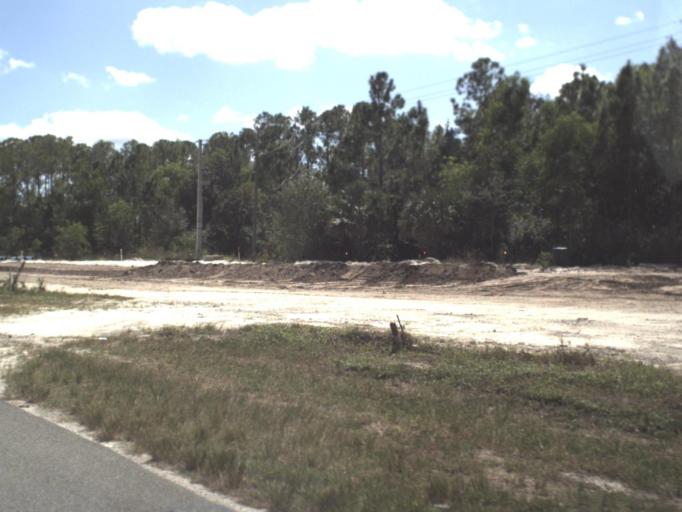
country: US
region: Florida
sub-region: Collier County
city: Lely Resort
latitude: 26.0477
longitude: -81.6746
